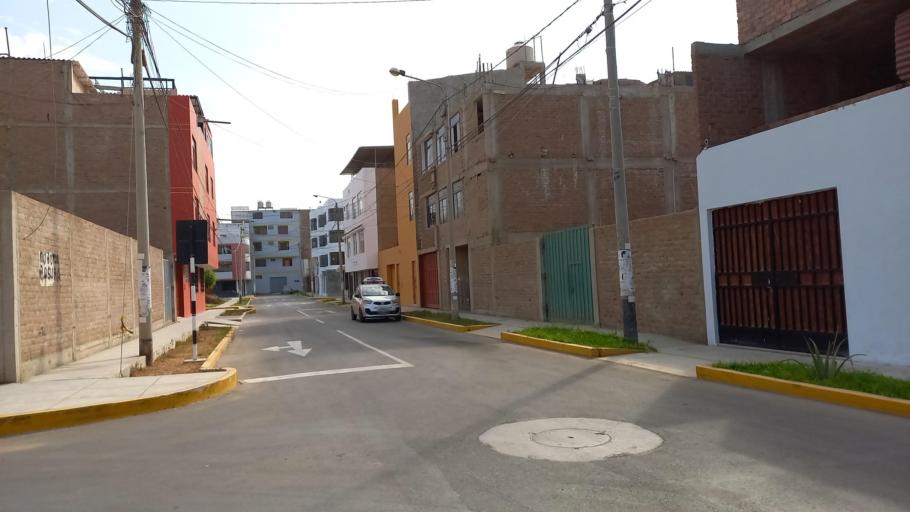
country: PE
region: La Libertad
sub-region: Provincia de Trujillo
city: Trujillo
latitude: -8.1171
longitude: -79.0455
